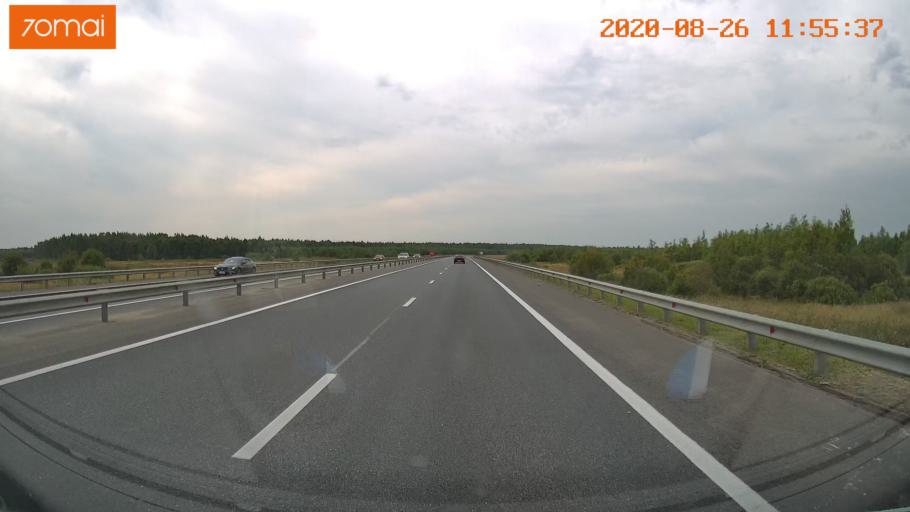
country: RU
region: Rjazan
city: Kiritsy
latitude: 54.2706
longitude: 40.3934
